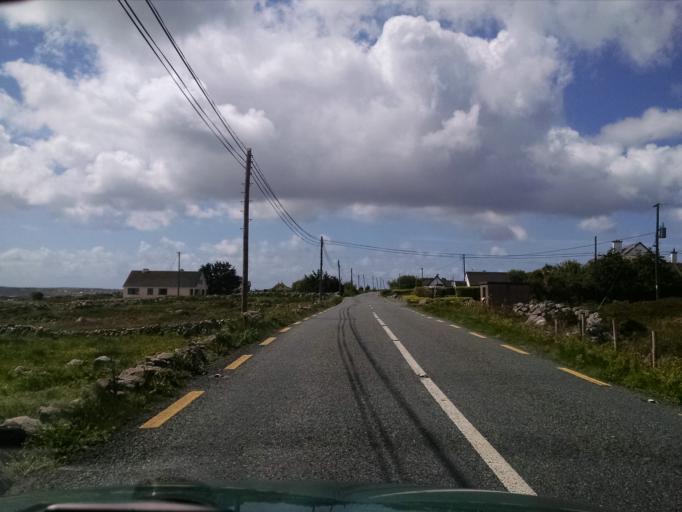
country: IE
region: Connaught
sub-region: County Galway
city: Oughterard
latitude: 53.2989
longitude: -9.6388
